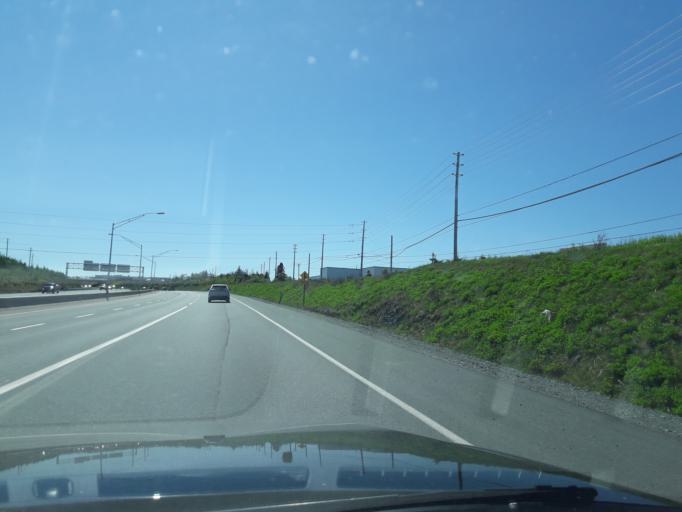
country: CA
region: Newfoundland and Labrador
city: St. John's
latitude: 47.6129
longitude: -52.7151
